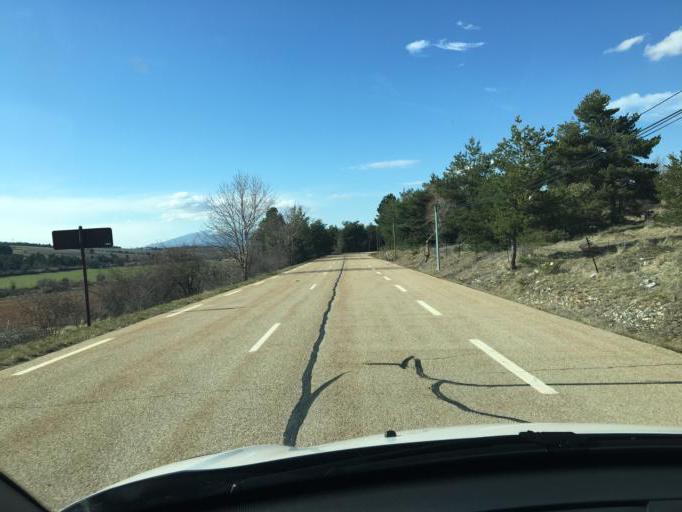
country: FR
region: Provence-Alpes-Cote d'Azur
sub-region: Departement du Vaucluse
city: Sault
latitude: 44.0191
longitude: 5.4711
